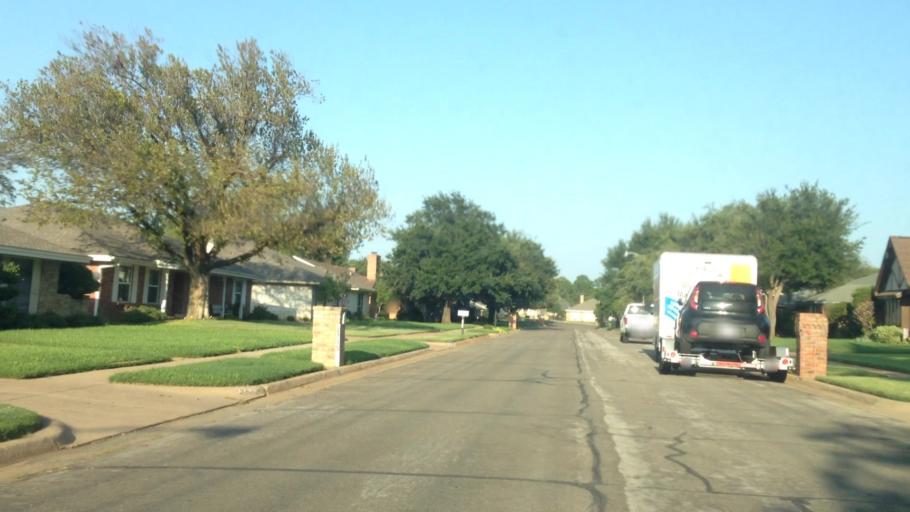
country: US
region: Texas
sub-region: Tarrant County
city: Pantego
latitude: 32.7203
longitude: -97.1597
